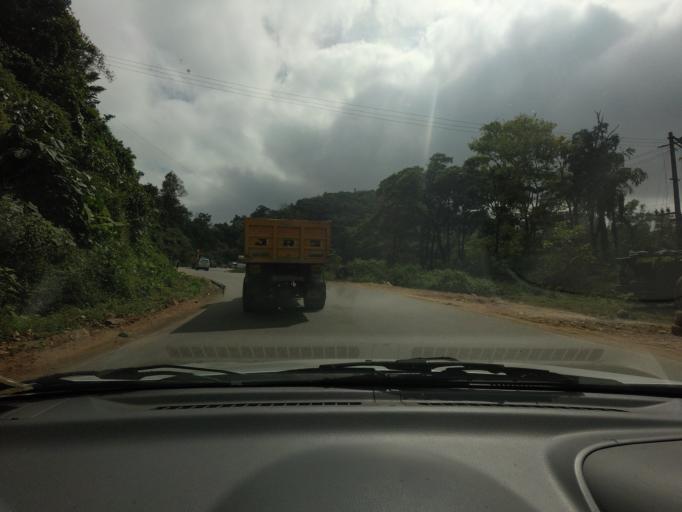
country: IN
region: Karnataka
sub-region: Hassan
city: Sakleshpur
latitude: 12.9201
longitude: 75.7571
